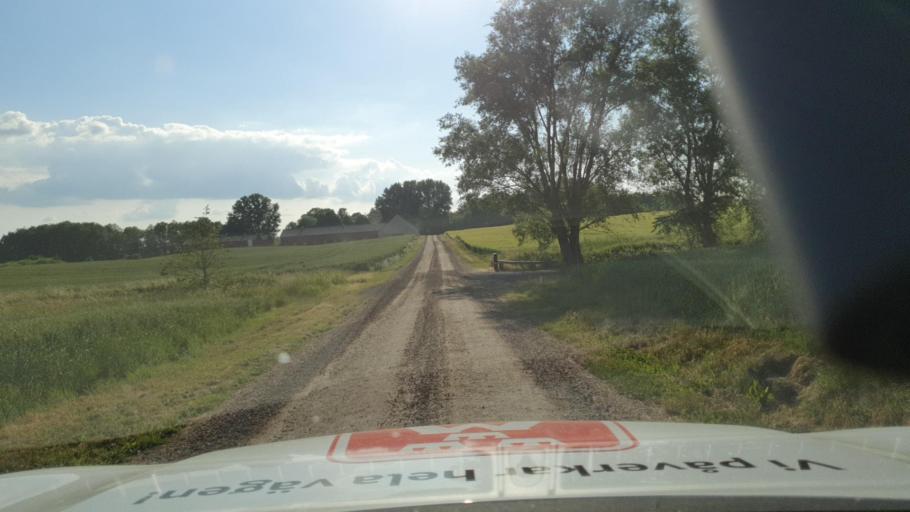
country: SE
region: Skane
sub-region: Skurups Kommun
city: Rydsgard
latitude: 55.4901
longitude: 13.5822
